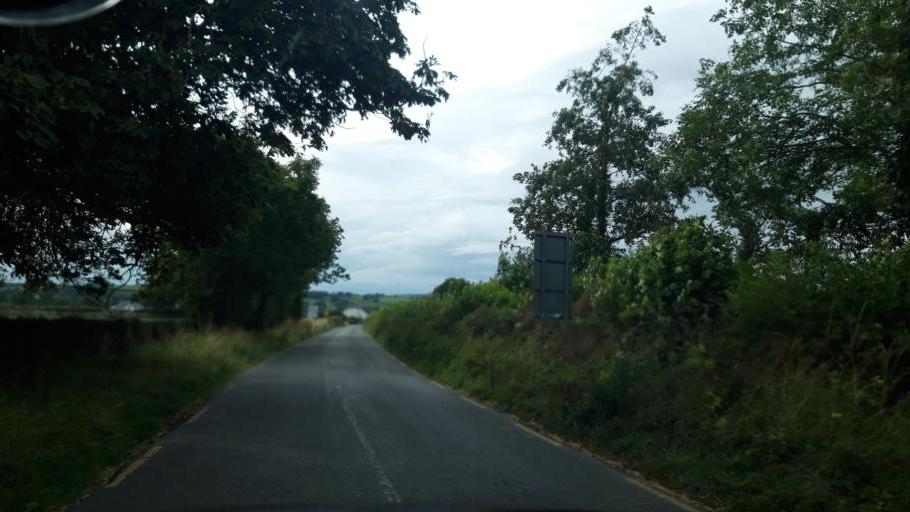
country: IE
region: Leinster
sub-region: Kilkenny
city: Ballyragget
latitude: 52.7577
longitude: -7.3765
